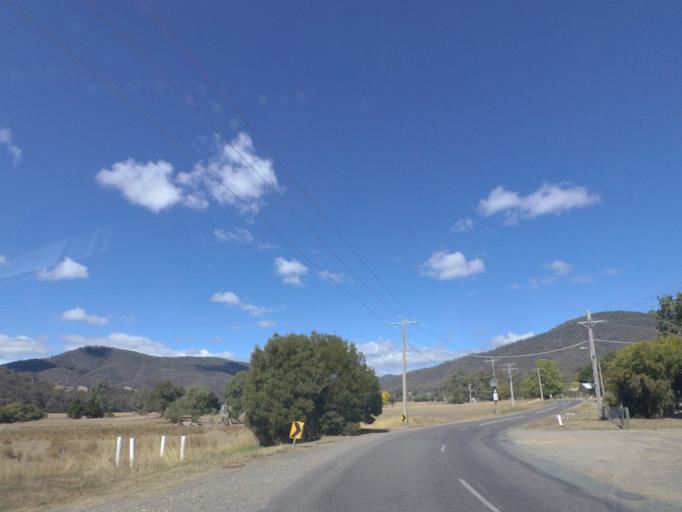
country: AU
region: Victoria
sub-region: Murrindindi
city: Alexandra
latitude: -37.2925
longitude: 145.8191
